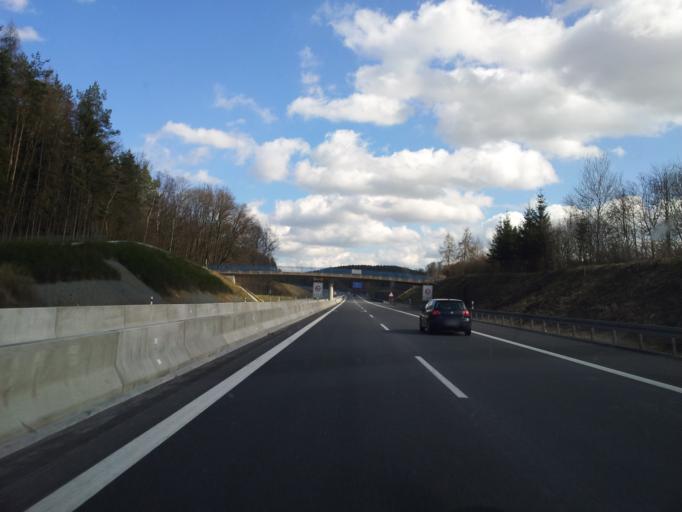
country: DE
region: Bavaria
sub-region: Upper Franconia
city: Harsdorf
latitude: 50.0315
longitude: 11.5674
